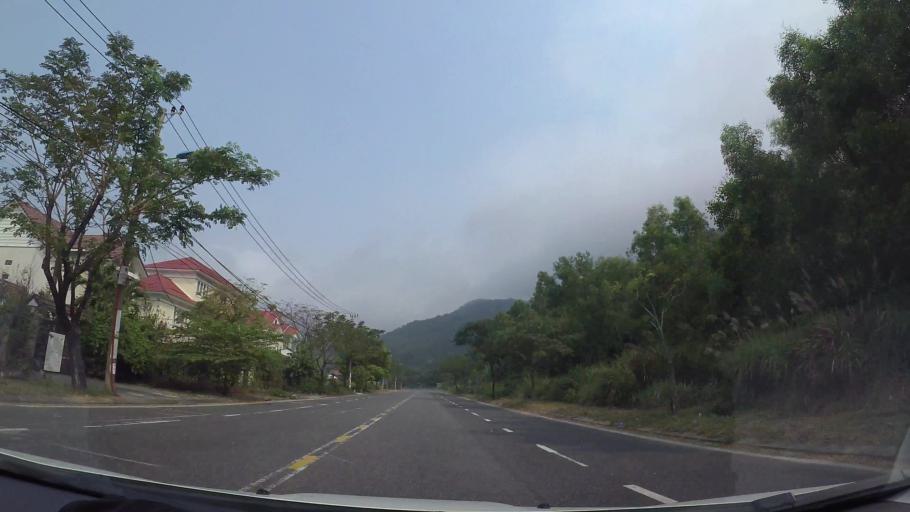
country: VN
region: Da Nang
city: Son Tra
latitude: 16.1040
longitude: 108.2642
